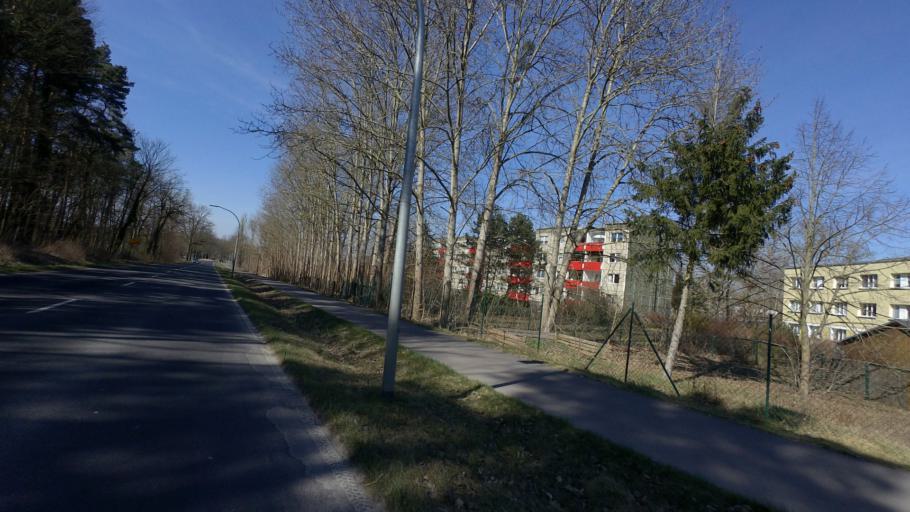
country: DE
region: Brandenburg
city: Muncheberg
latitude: 52.5166
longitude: 14.1118
